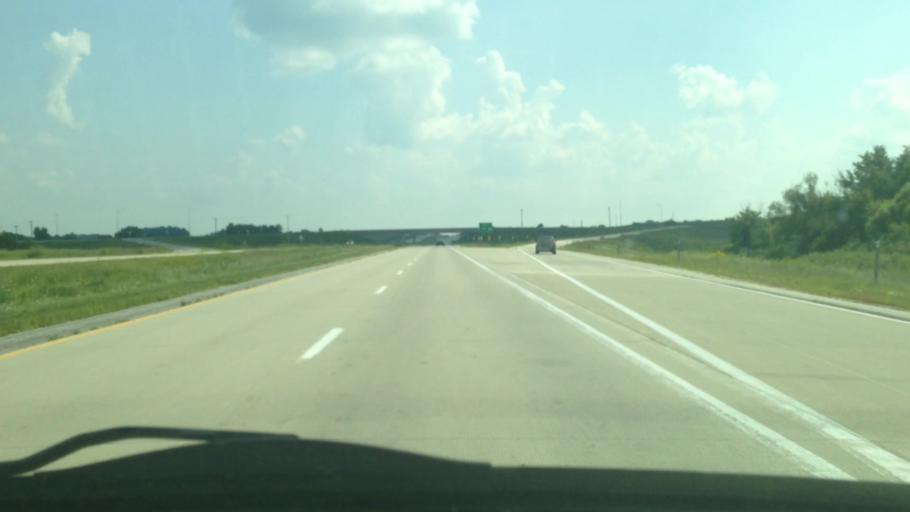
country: US
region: Iowa
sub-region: Bremer County
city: Denver
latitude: 42.7192
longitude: -92.3374
